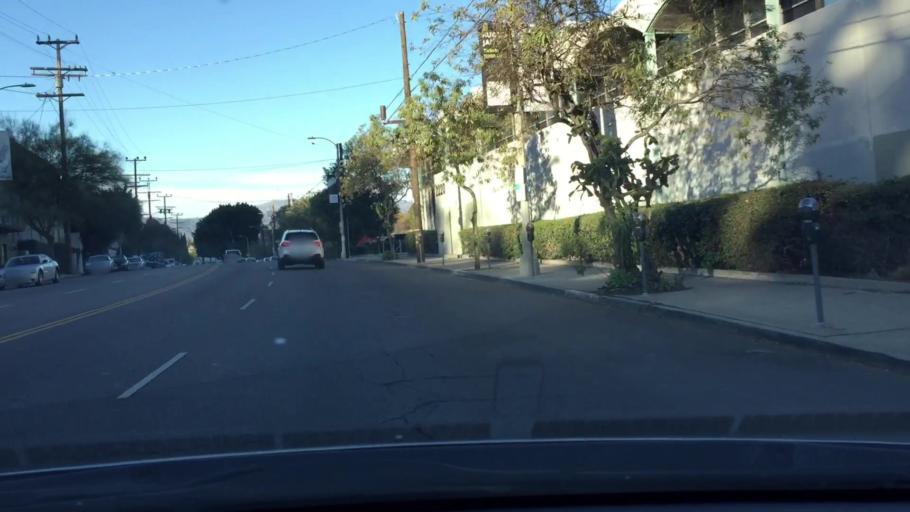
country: US
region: California
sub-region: Los Angeles County
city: Silver Lake
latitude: 34.1001
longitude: -118.2734
